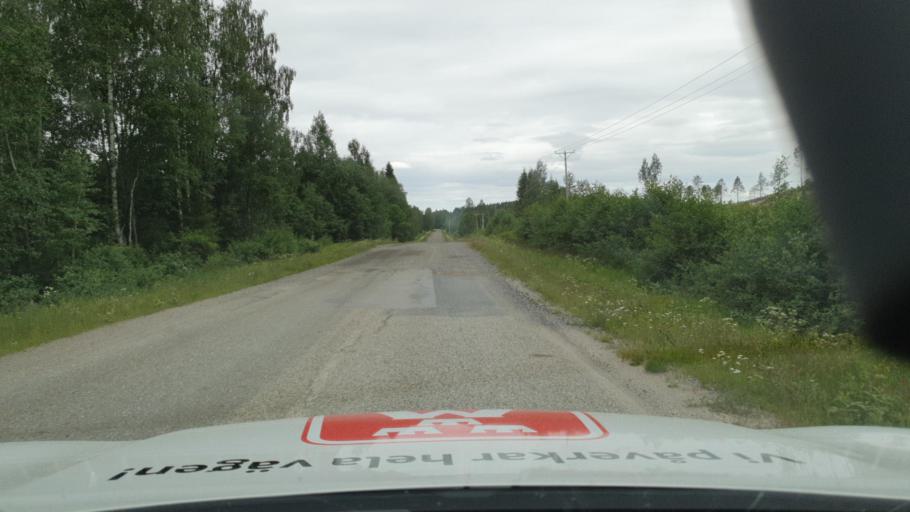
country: SE
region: Vaesterbotten
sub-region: Nordmalings Kommun
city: Nordmaling
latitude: 63.7746
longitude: 19.4066
